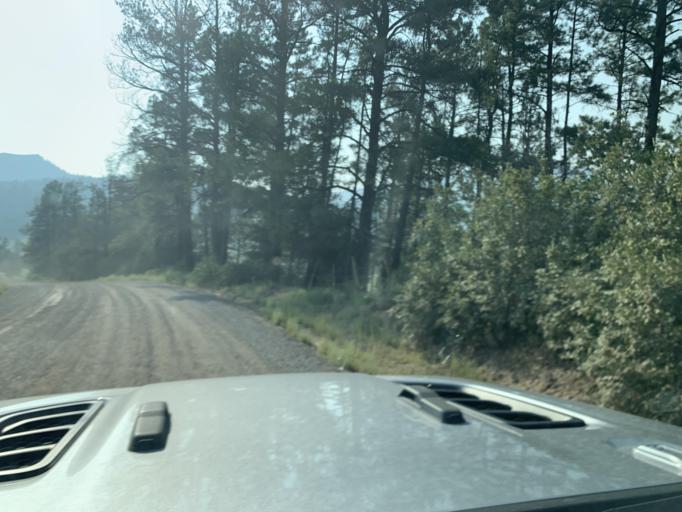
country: US
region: Colorado
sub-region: Archuleta County
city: Pagosa Springs
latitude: 37.2235
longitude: -107.2110
